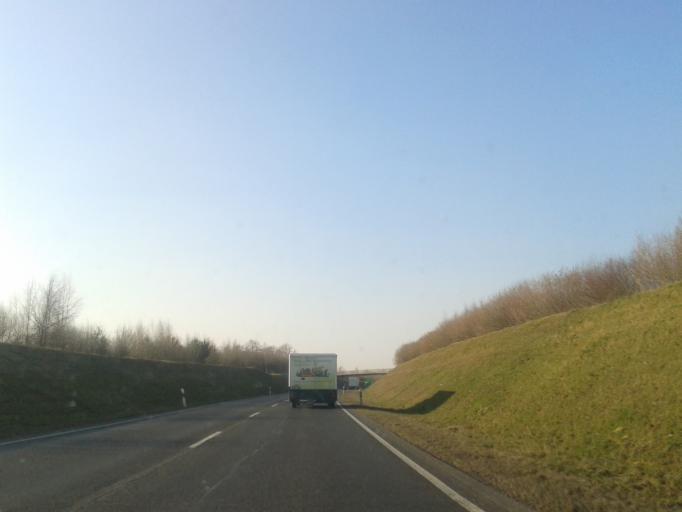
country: DE
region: Saxony
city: Nossen
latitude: 51.0276
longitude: 13.2981
